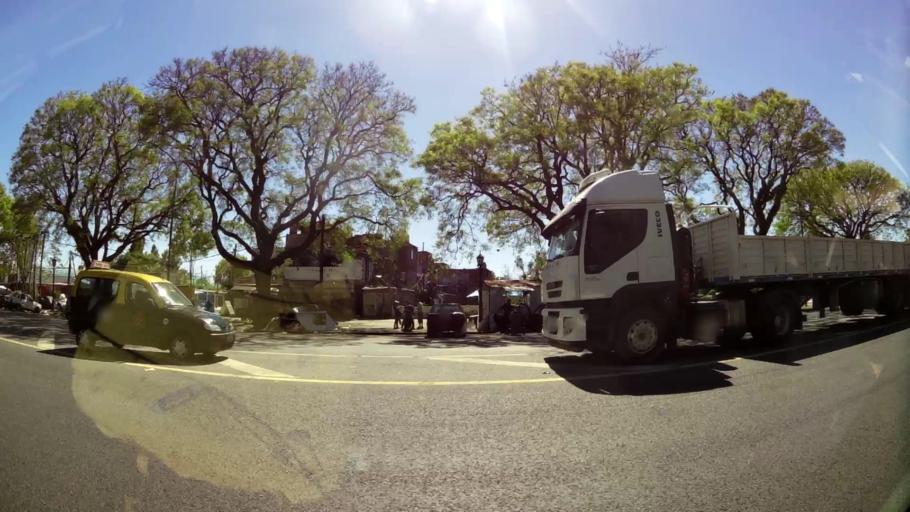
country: AR
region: Buenos Aires F.D.
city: Buenos Aires
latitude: -34.6196
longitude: -58.3555
